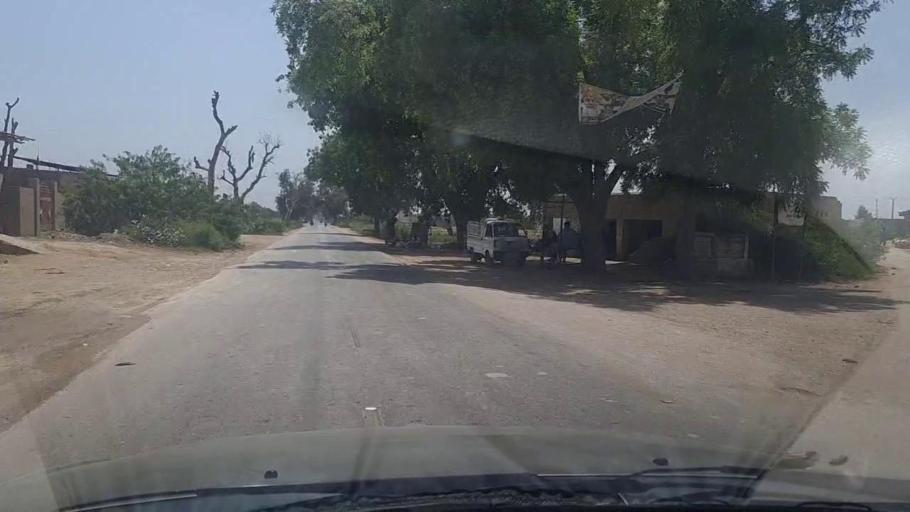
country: PK
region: Sindh
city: Tando Jam
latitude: 25.3721
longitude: 68.4701
